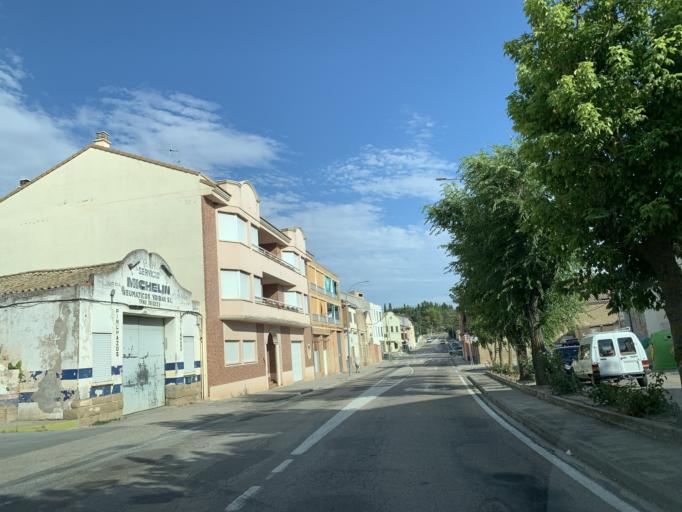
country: ES
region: Aragon
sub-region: Provincia de Huesca
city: Ayerbe
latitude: 42.2747
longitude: -0.6860
